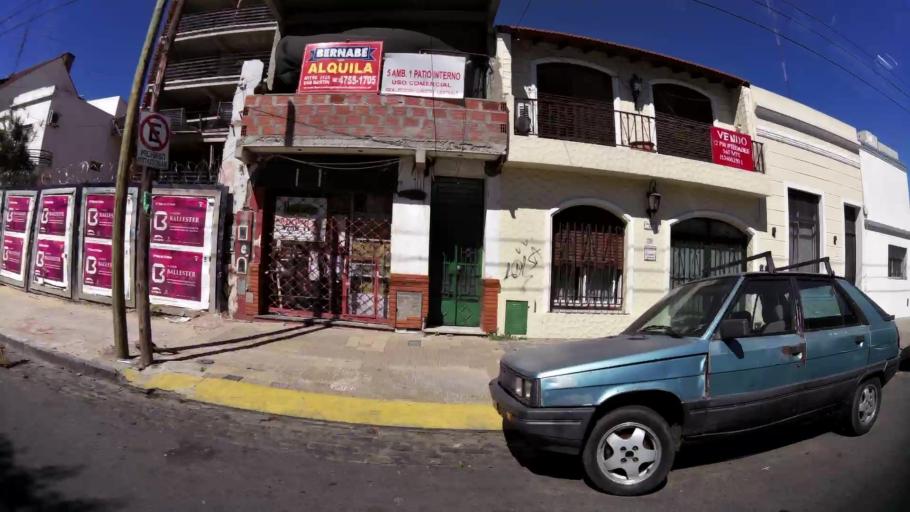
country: AR
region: Buenos Aires
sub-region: Partido de General San Martin
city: General San Martin
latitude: -34.5725
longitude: -58.5364
